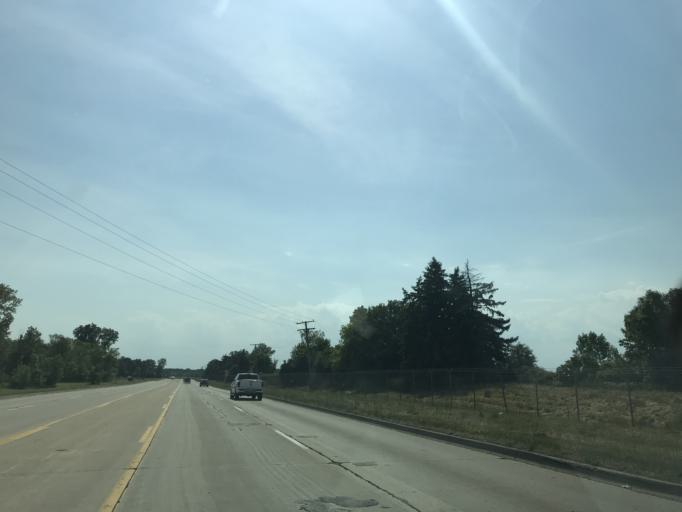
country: US
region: Michigan
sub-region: Wayne County
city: Romulus
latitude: 42.1948
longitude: -83.3428
